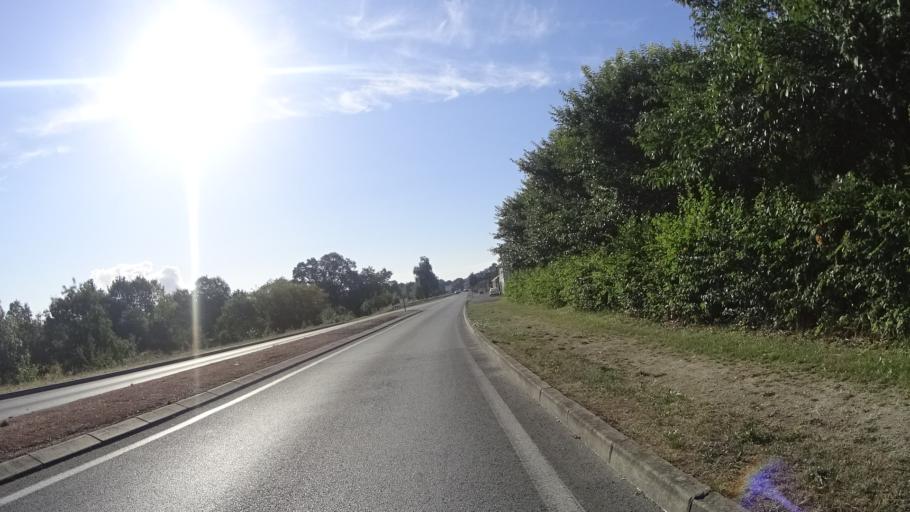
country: FR
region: Pays de la Loire
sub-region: Departement de Maine-et-Loire
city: Varennes-sur-Loire
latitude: 47.2202
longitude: 0.0456
